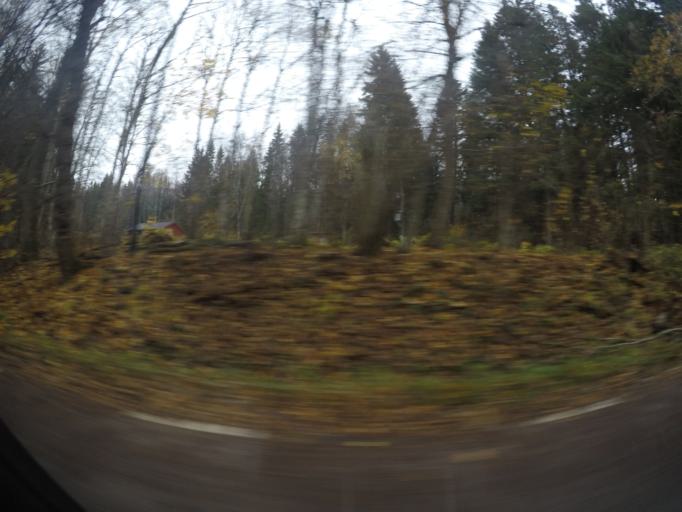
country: SE
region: Vaestmanland
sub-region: Surahammars Kommun
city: Ramnas
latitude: 59.6927
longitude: 16.0814
